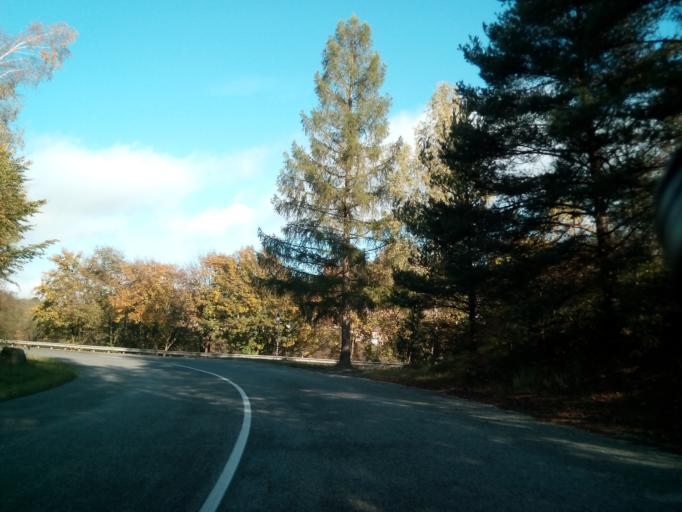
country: SK
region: Kosicky
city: Gelnica
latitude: 48.8880
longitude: 21.0066
